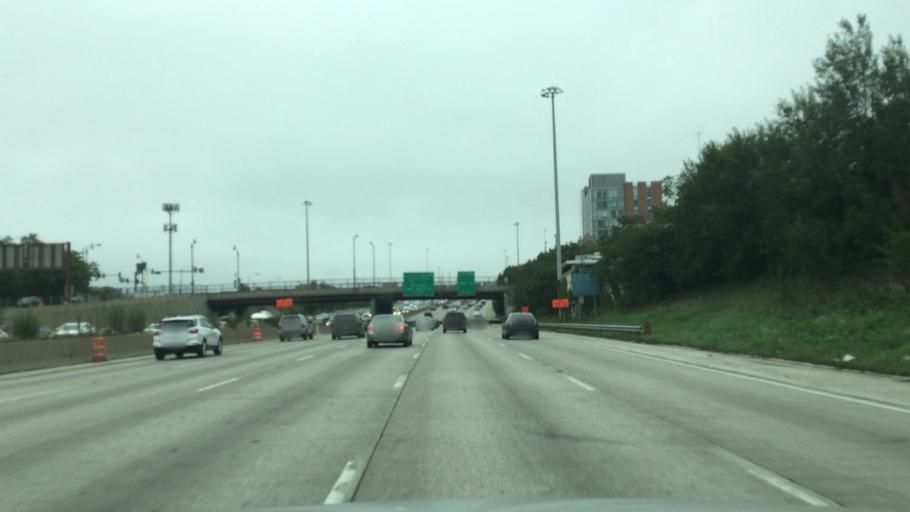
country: US
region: Illinois
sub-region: Cook County
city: Chicago
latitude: 41.8689
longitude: -87.6450
